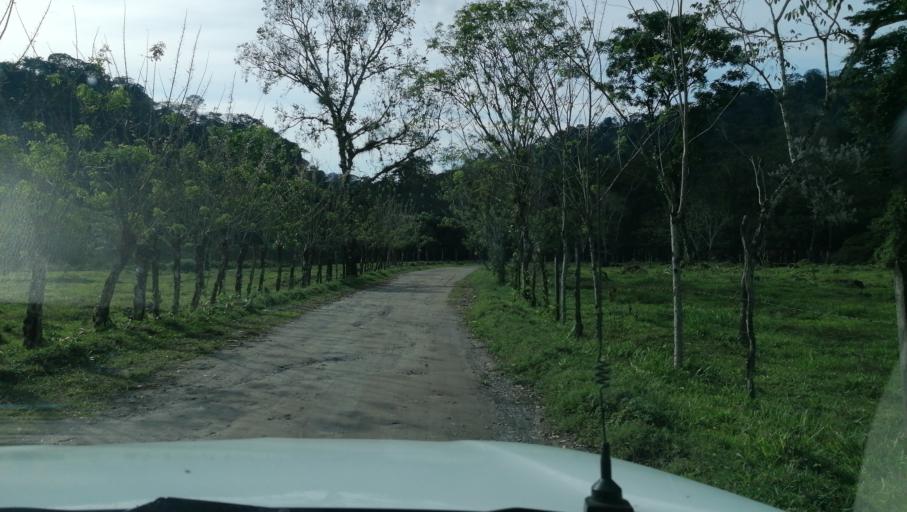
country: MX
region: Chiapas
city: Ostuacan
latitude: 17.4725
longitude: -93.2377
